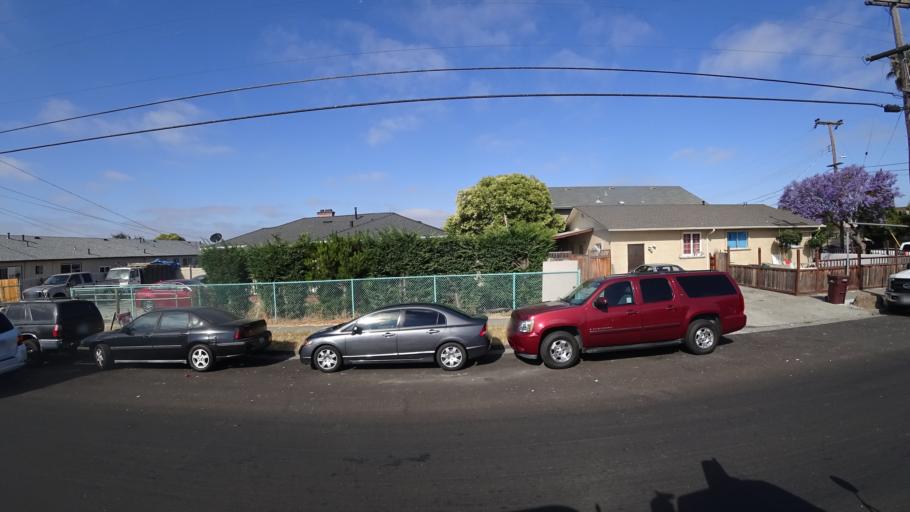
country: US
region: California
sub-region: Alameda County
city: Hayward
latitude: 37.6398
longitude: -122.0733
